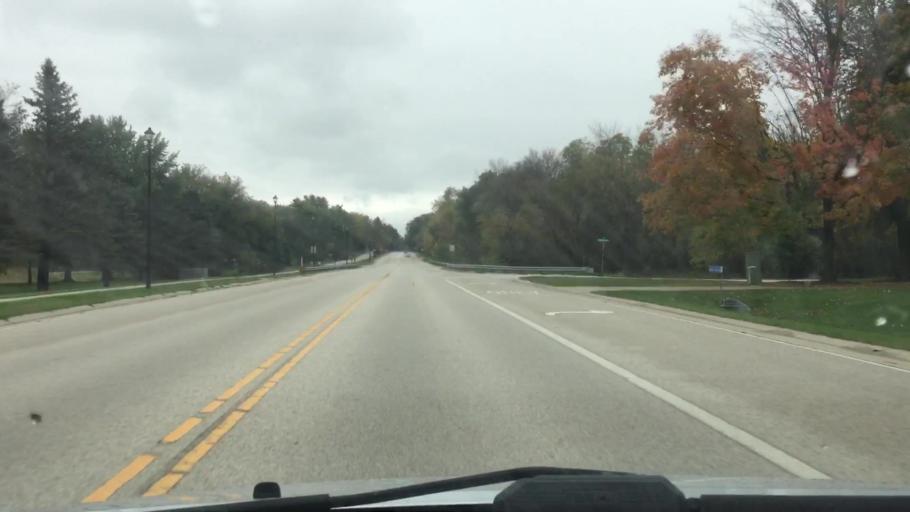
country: US
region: Wisconsin
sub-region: Waukesha County
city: Oconomowoc
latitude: 43.1293
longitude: -88.4999
